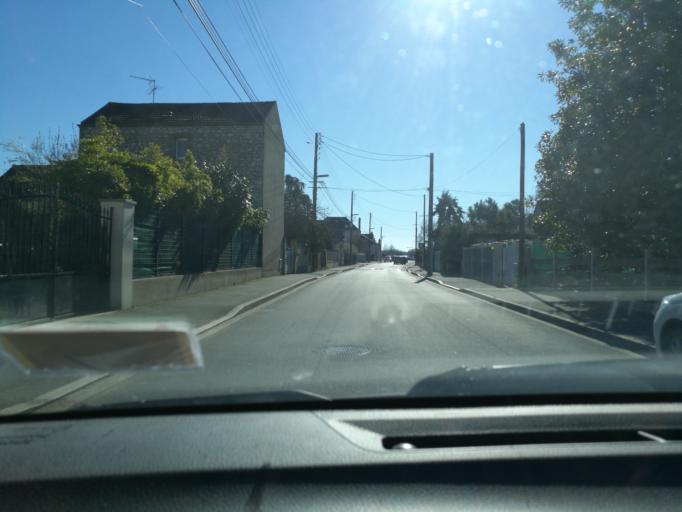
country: FR
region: Centre
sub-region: Departement du Loiret
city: Saint-Pryve-Saint-Mesmin
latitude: 47.8860
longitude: 1.8877
